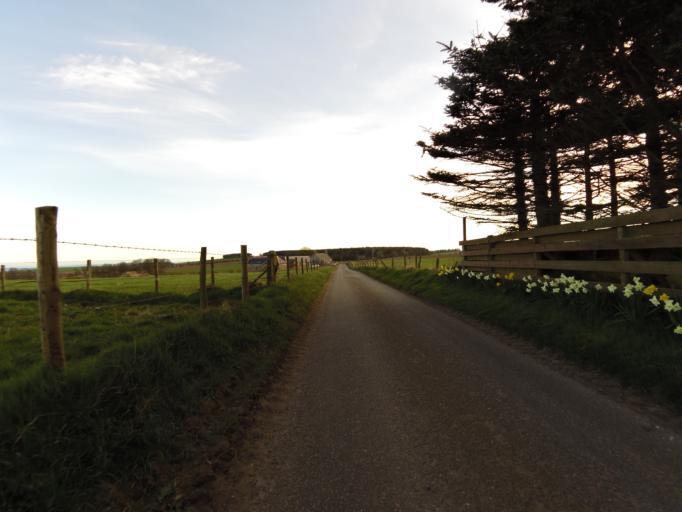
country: GB
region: Scotland
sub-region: Aberdeenshire
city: Stonehaven
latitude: 56.9328
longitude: -2.2255
